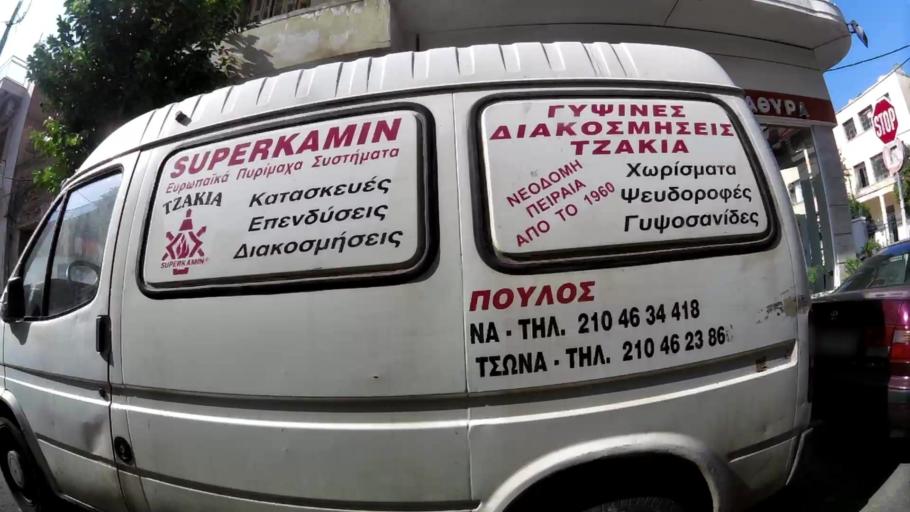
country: GR
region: Attica
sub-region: Nomos Piraios
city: Drapetsona
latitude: 37.9513
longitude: 23.6299
